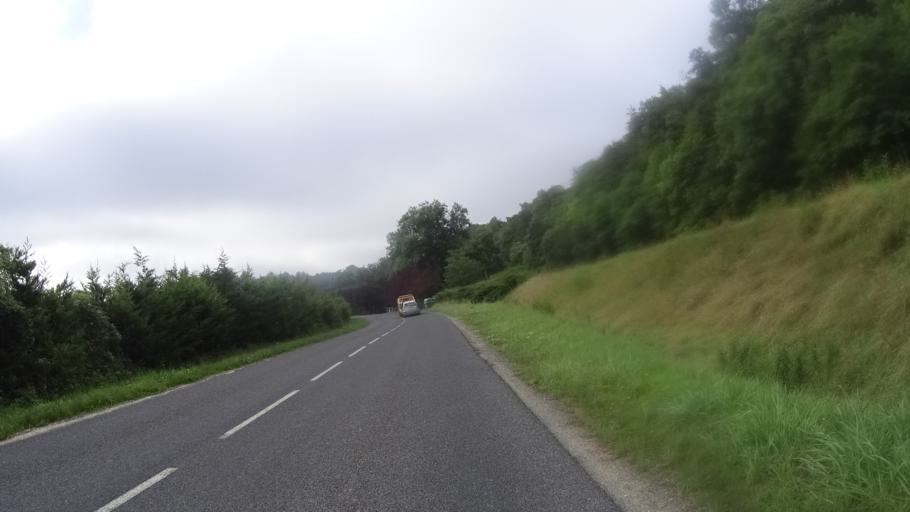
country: FR
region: Lorraine
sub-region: Departement de la Meuse
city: Fains-Veel
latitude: 48.7991
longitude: 5.1123
